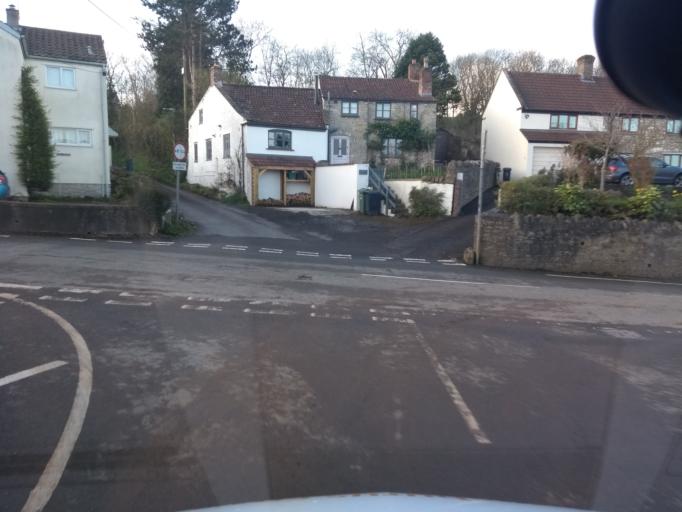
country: GB
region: England
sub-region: Somerset
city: Wedmore
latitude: 51.2262
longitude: -2.8053
